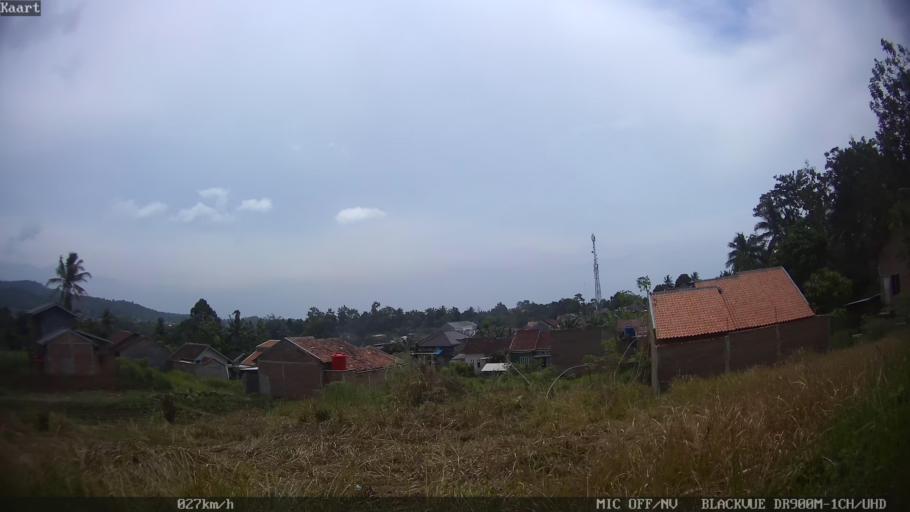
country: ID
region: Lampung
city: Bandarlampung
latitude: -5.4112
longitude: 105.2104
